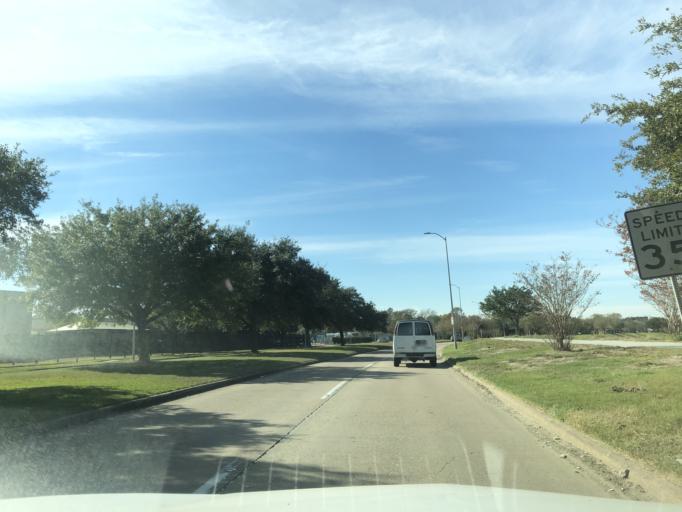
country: US
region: Texas
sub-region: Harris County
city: Bellaire
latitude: 29.6749
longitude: -95.4837
